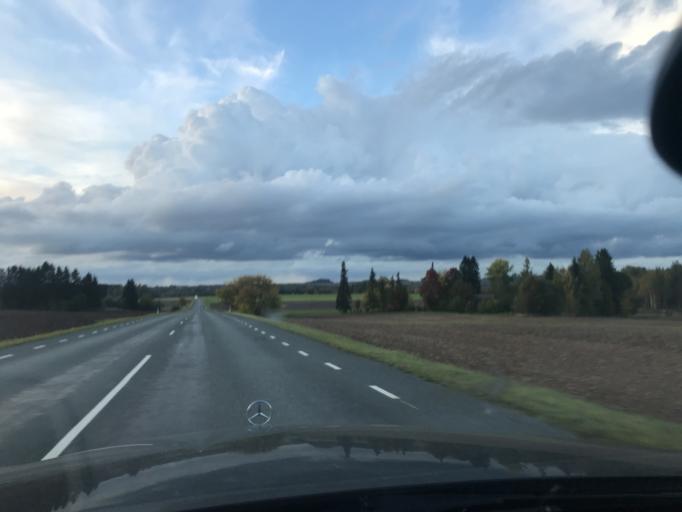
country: EE
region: Vorumaa
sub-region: Antsla vald
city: Vana-Antsla
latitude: 57.9182
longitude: 26.3510
